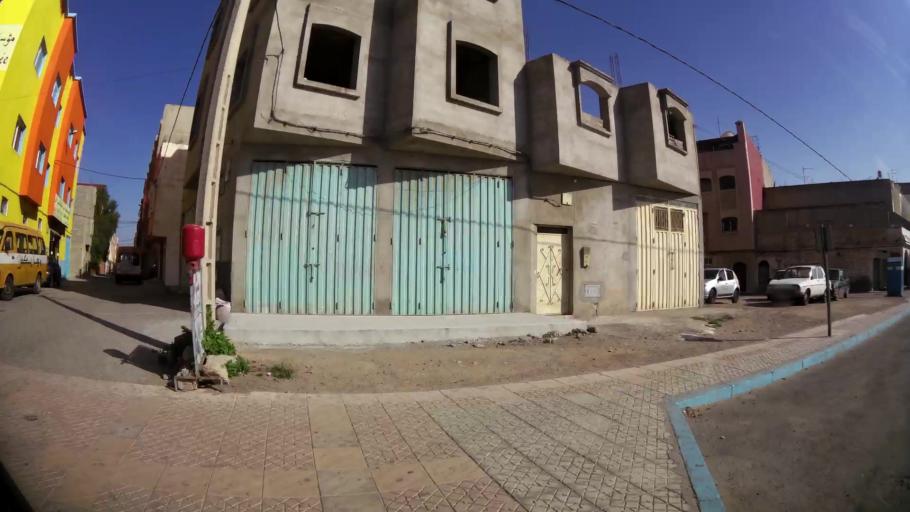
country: MA
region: Souss-Massa-Draa
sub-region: Inezgane-Ait Mellou
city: Inezgane
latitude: 30.3733
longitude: -9.5304
